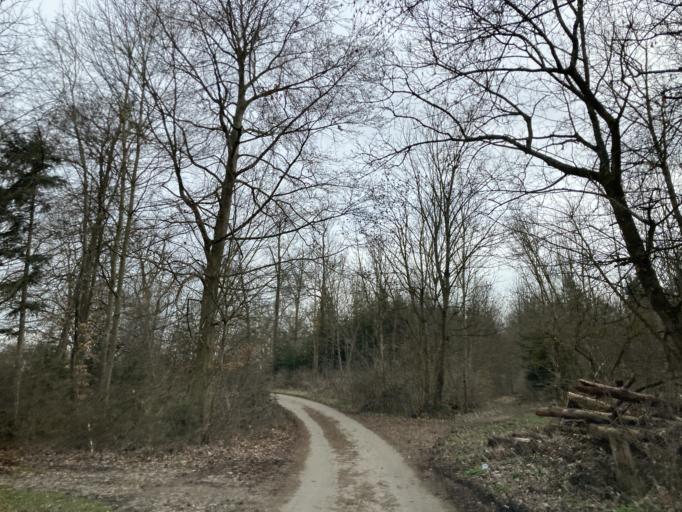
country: DE
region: Baden-Wuerttemberg
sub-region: Tuebingen Region
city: Rottenburg
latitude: 48.4569
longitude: 8.9056
